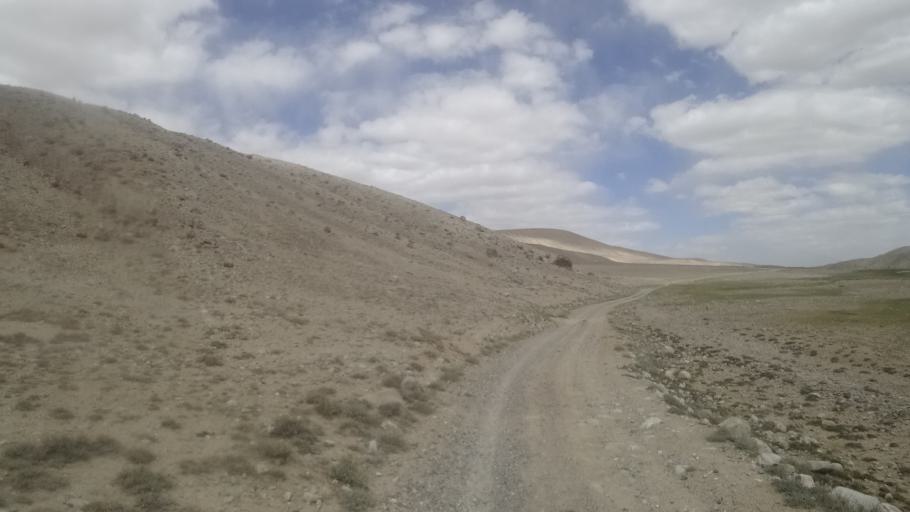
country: AF
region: Badakhshan
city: Khandud
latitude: 37.4084
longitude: 73.1549
